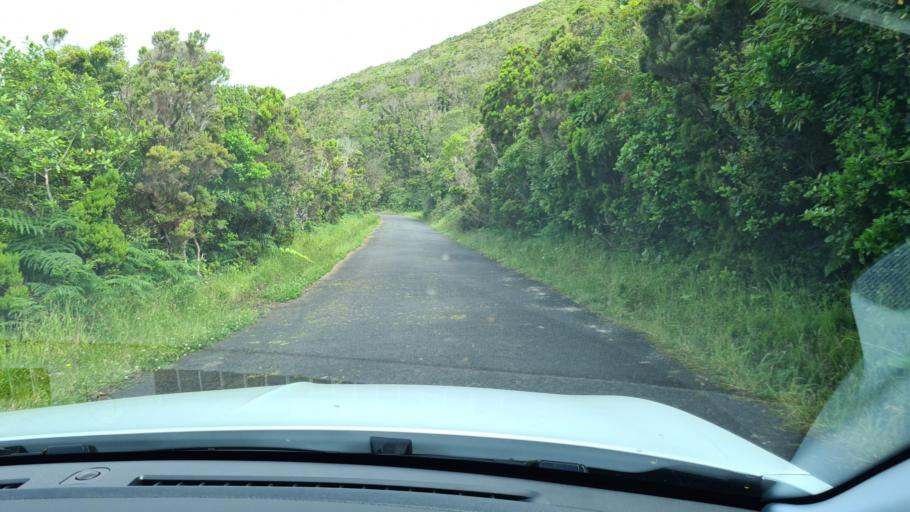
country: PT
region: Azores
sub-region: Sao Roque do Pico
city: Sao Roque do Pico
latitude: 38.6598
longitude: -28.1205
